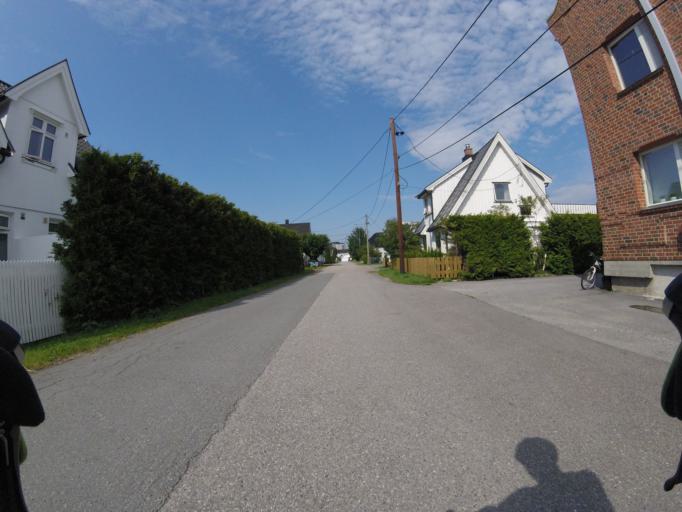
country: NO
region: Akershus
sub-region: Skedsmo
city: Lillestrom
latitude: 59.9560
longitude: 11.0633
